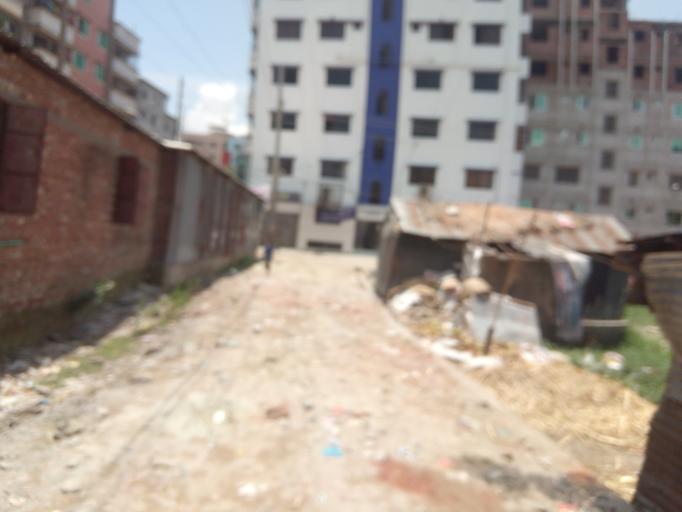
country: BD
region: Dhaka
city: Paltan
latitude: 23.7562
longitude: 90.4411
